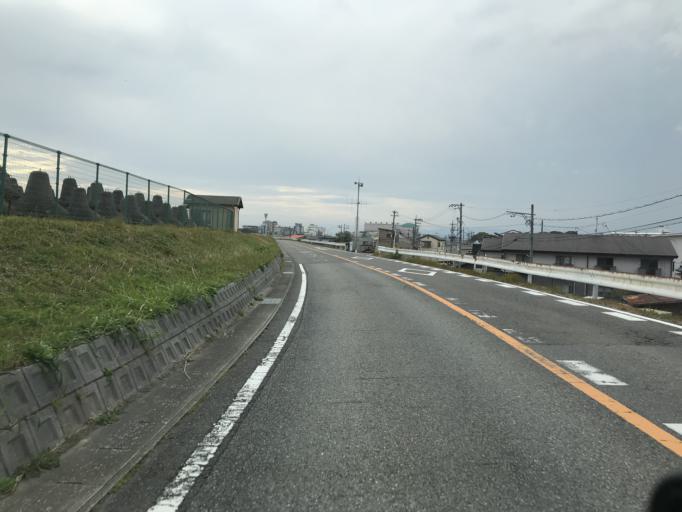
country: JP
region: Aichi
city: Nagoya-shi
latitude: 35.1922
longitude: 136.8576
